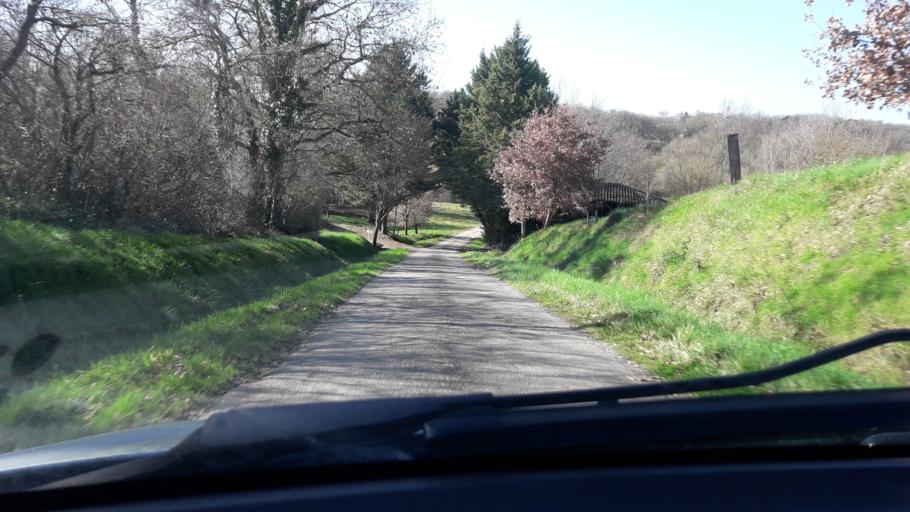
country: FR
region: Midi-Pyrenees
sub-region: Departement du Gers
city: Gimont
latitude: 43.6437
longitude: 1.0129
